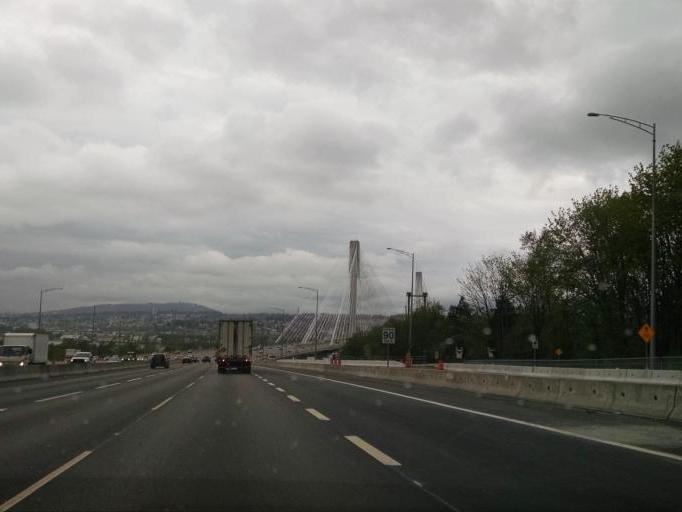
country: CA
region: British Columbia
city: Port Moody
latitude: 49.2094
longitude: -122.8061
